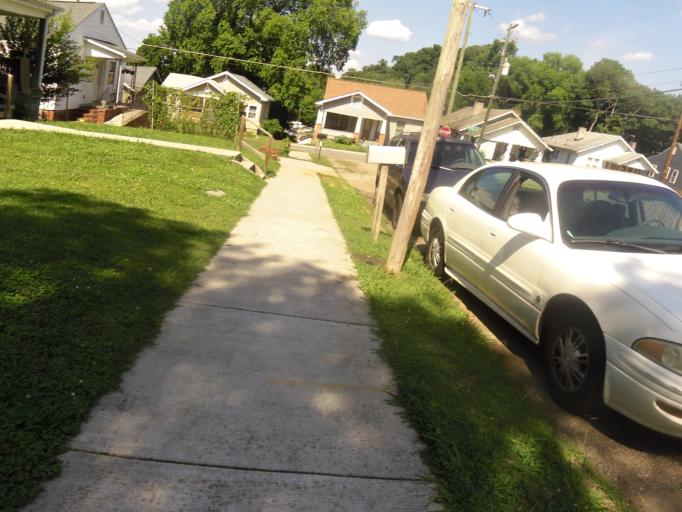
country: US
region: Tennessee
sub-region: Knox County
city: Knoxville
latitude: 35.9560
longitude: -83.9101
